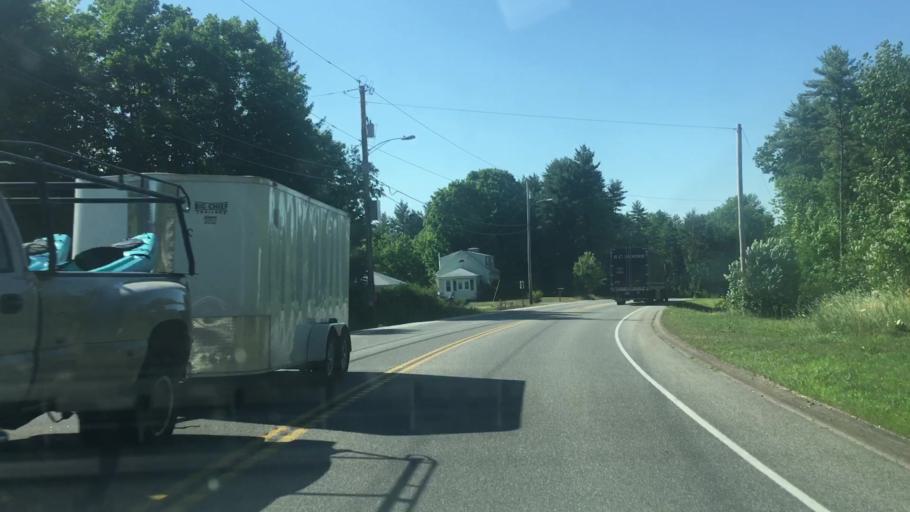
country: US
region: Maine
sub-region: York County
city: Buxton
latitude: 43.5713
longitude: -70.5117
